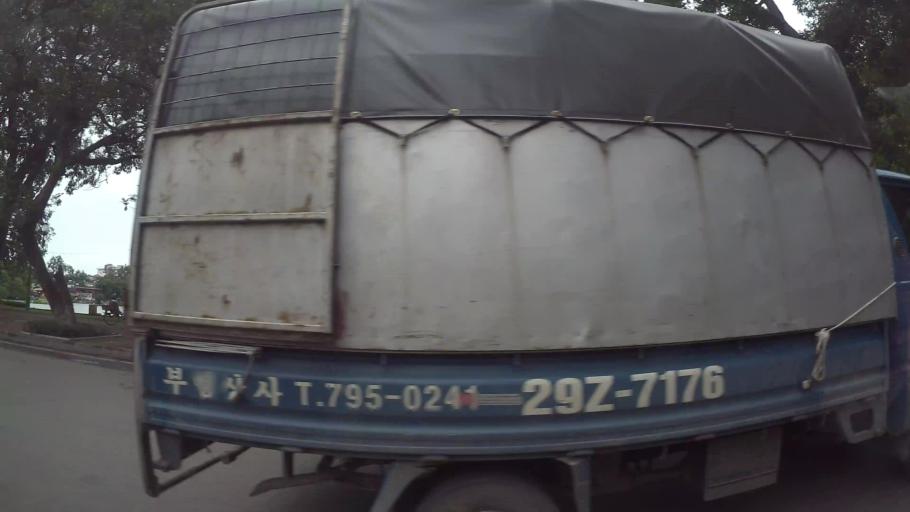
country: VN
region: Ha Noi
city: Hai BaTrung
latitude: 21.0172
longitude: 105.8463
